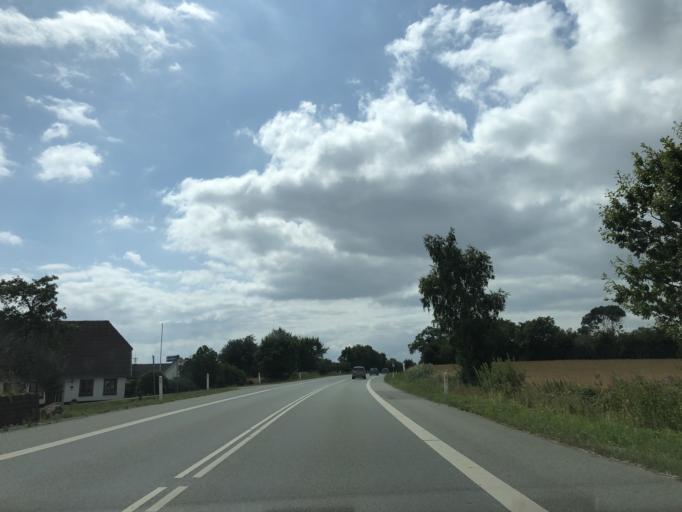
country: DK
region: South Denmark
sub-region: Sonderborg Kommune
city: Augustenborg
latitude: 54.9625
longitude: 9.9209
